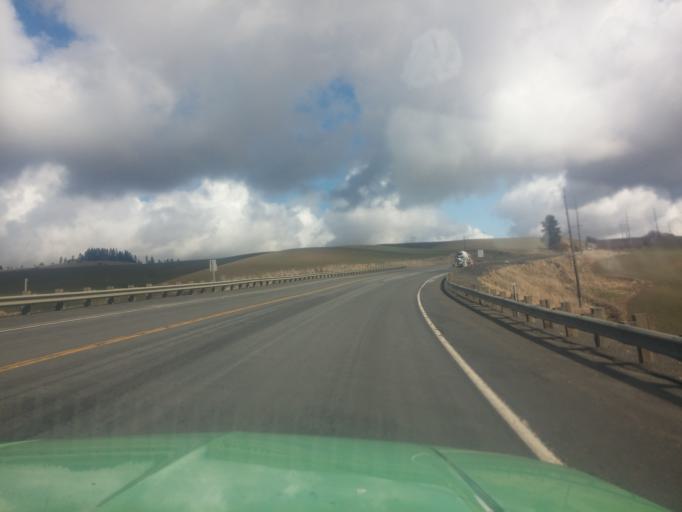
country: US
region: Idaho
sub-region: Latah County
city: Moscow
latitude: 46.8579
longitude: -117.0214
